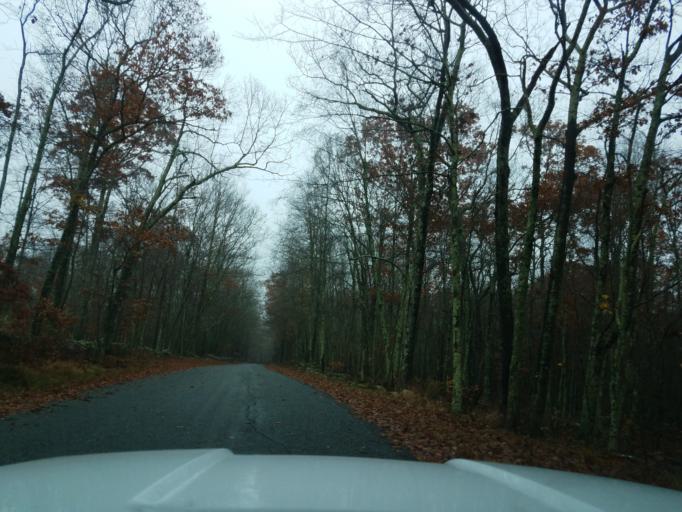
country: US
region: Connecticut
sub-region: Windham County
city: Windham
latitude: 41.7942
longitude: -72.1083
